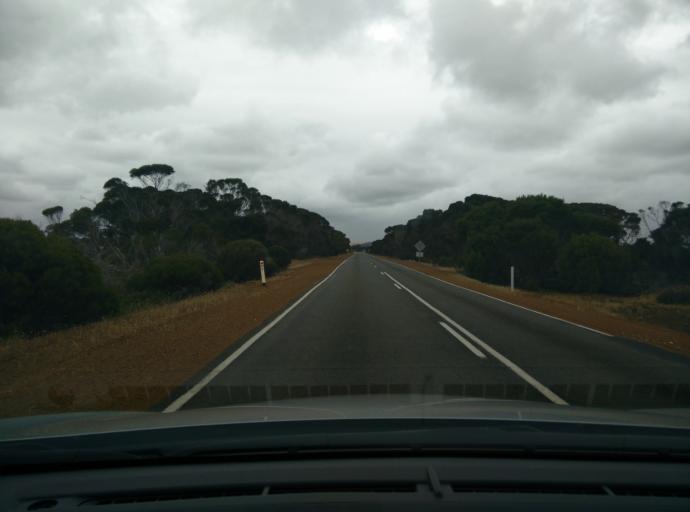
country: AU
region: South Australia
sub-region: Kangaroo Island
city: Kingscote
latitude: -35.7202
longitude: 137.5599
